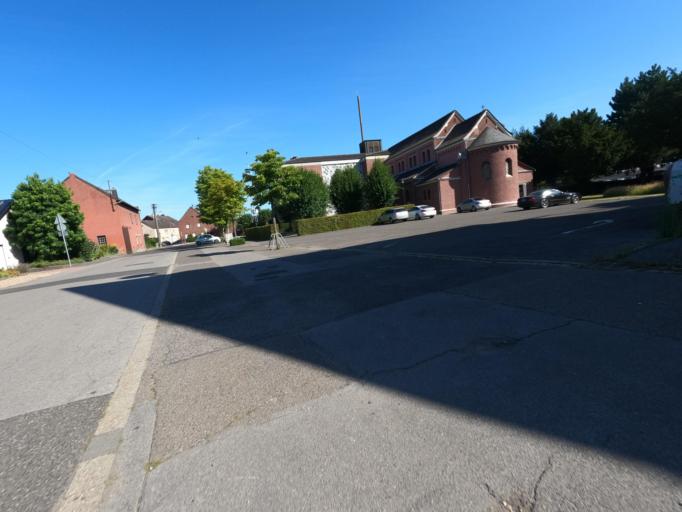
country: DE
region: North Rhine-Westphalia
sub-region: Regierungsbezirk Koln
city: Heinsberg
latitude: 51.0735
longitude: 6.1282
